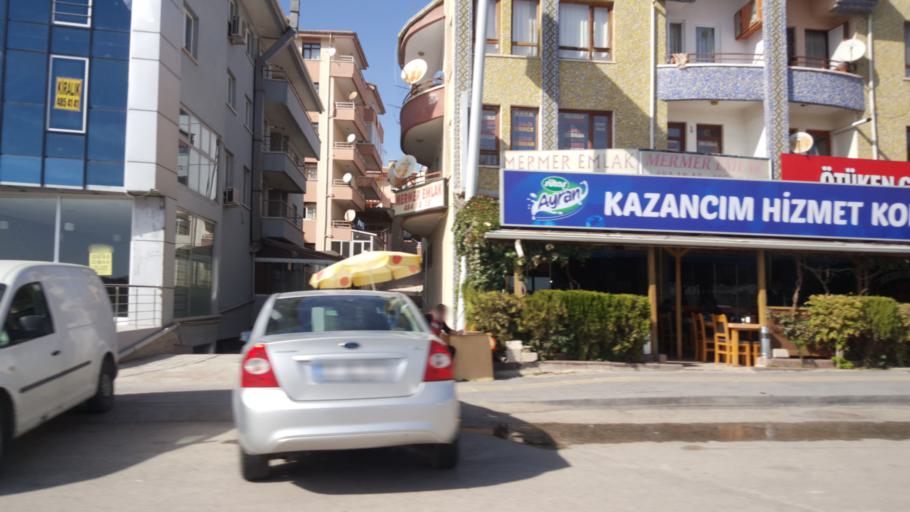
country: TR
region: Ankara
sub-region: Goelbasi
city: Golbasi
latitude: 39.8040
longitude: 32.8013
